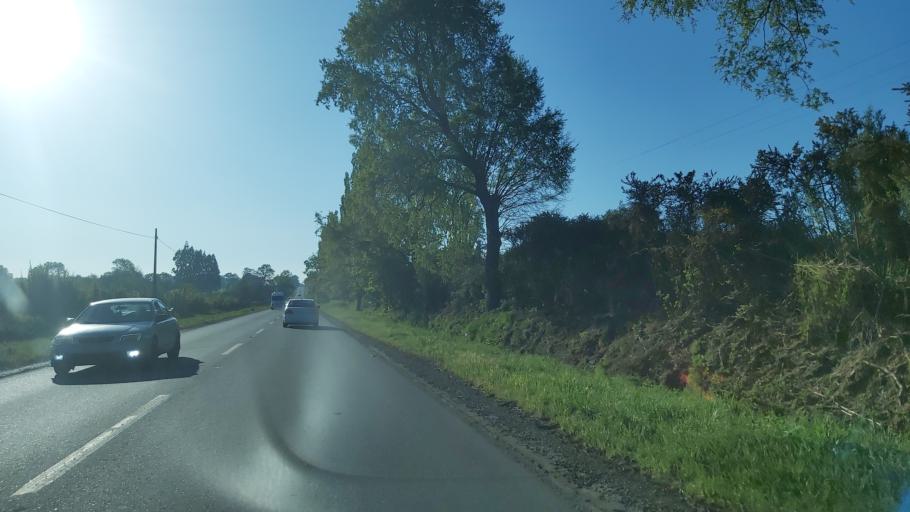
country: CL
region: Araucania
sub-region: Provincia de Malleco
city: Victoria
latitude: -38.2592
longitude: -72.2571
